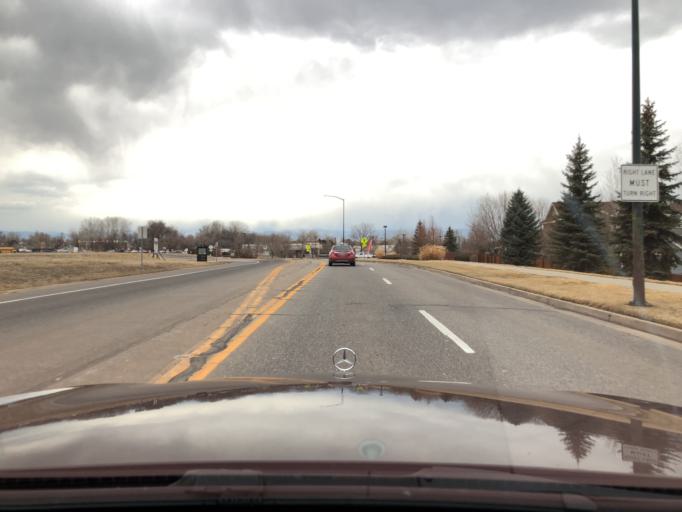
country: US
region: Colorado
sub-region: Boulder County
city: Lafayette
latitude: 40.0149
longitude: -105.0986
